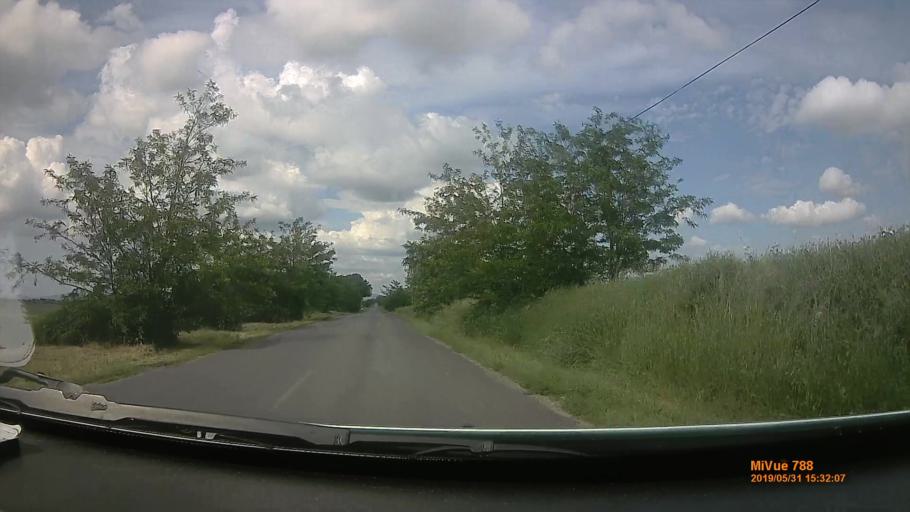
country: HU
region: Borsod-Abauj-Zemplen
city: Prugy
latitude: 48.0691
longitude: 21.2371
